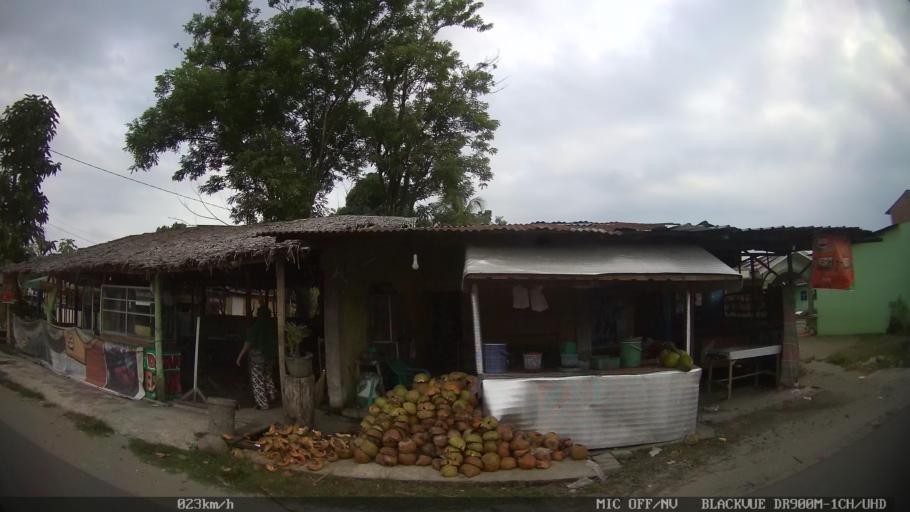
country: ID
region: North Sumatra
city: Sunggal
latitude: 3.5585
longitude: 98.5546
